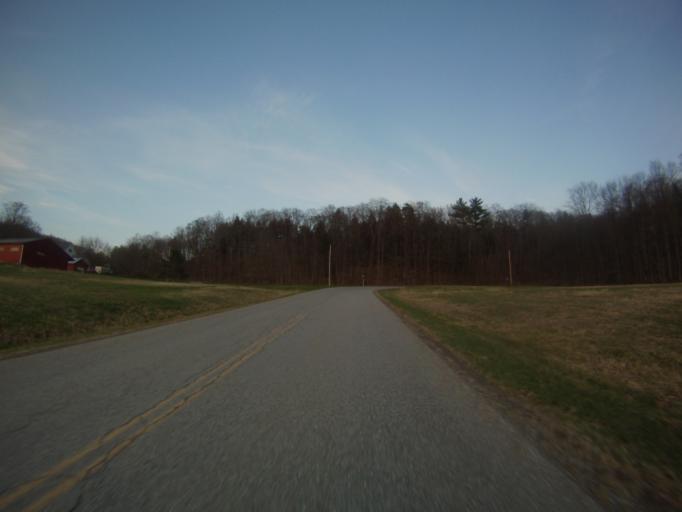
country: US
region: Vermont
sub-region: Addison County
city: Middlebury (village)
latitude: 44.0218
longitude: -73.2254
